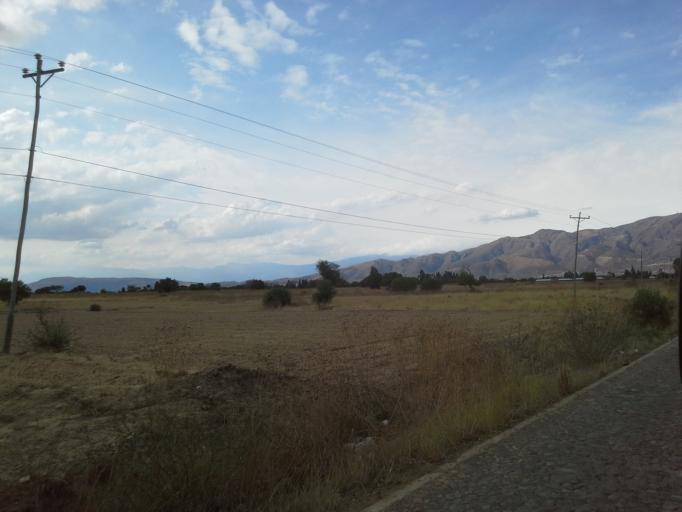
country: BO
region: Cochabamba
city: Tarata
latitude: -17.5997
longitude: -66.0188
